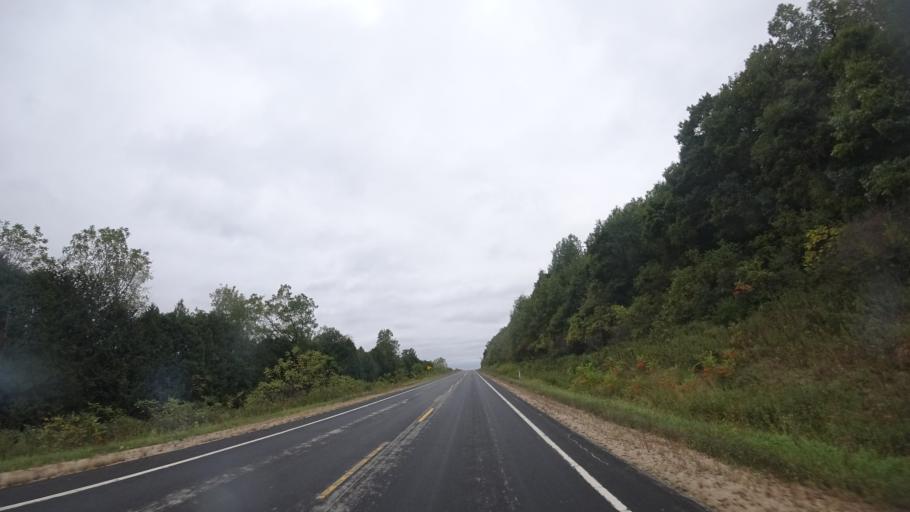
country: US
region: Wisconsin
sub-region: Grant County
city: Boscobel
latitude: 43.1985
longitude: -90.6533
